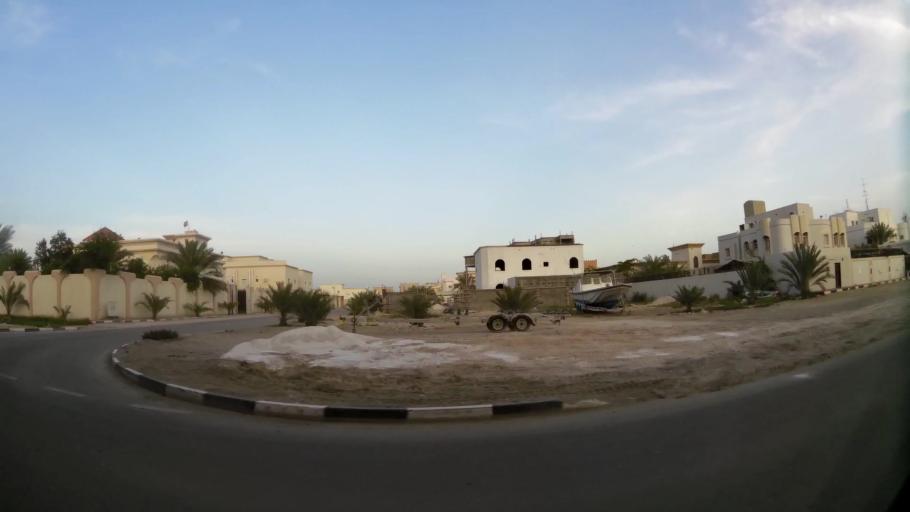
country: QA
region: Al Wakrah
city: Al Wakrah
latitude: 25.1835
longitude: 51.6108
